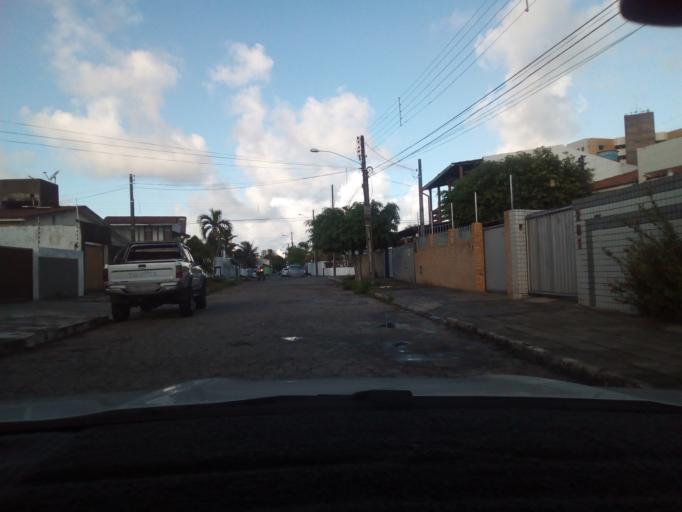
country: BR
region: Paraiba
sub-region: Joao Pessoa
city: Joao Pessoa
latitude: -7.1157
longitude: -34.8659
